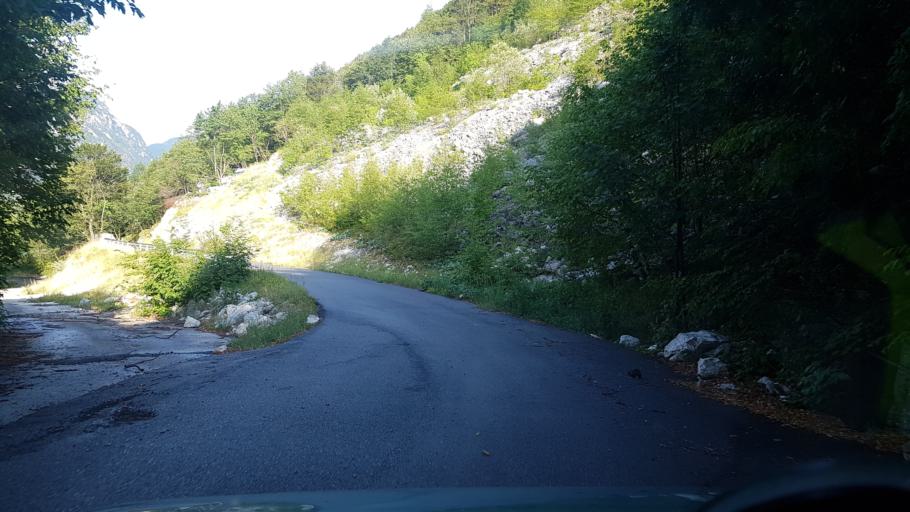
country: IT
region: Friuli Venezia Giulia
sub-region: Provincia di Udine
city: Lusevera
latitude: 46.3100
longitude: 13.2636
